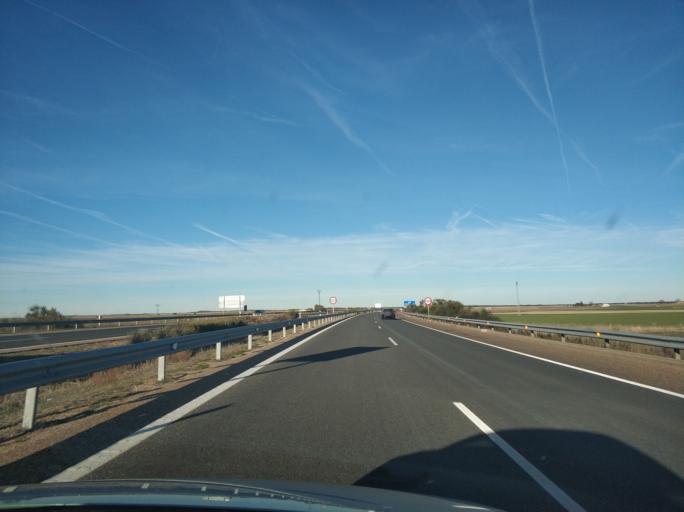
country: ES
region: Castille and Leon
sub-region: Provincia de Salamanca
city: Pajares de la Laguna
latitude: 41.0967
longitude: -5.5009
